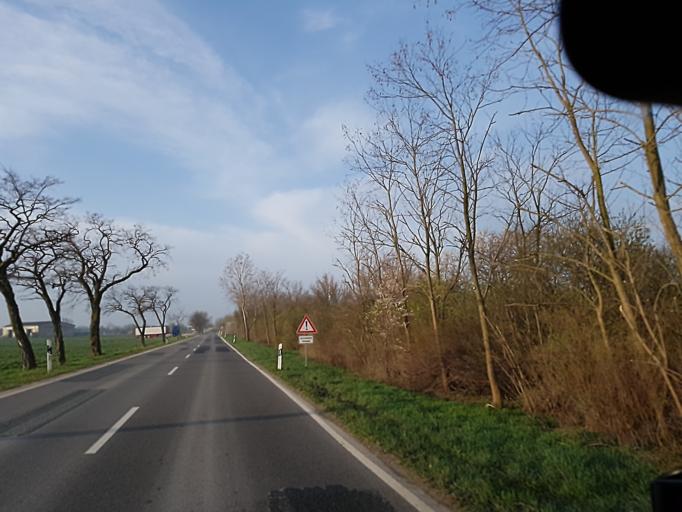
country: DE
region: Brandenburg
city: Muhlberg
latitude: 51.4292
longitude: 13.2679
